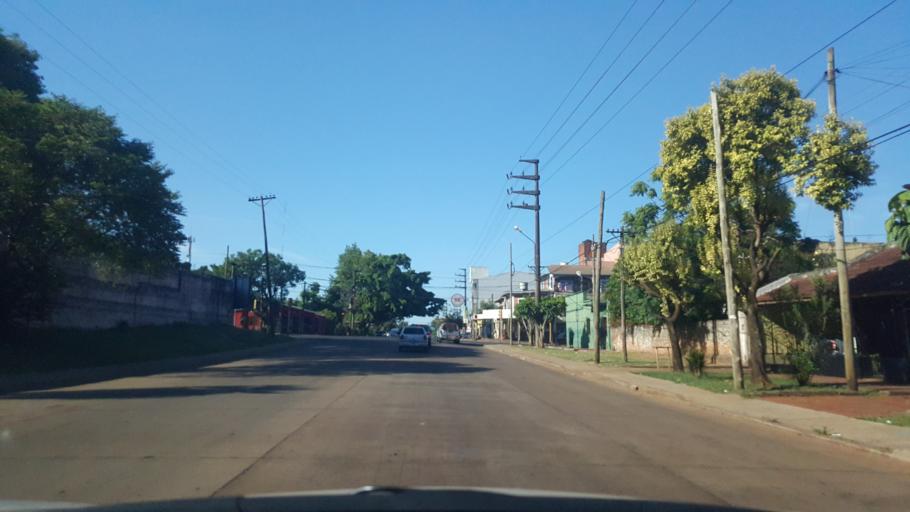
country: AR
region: Misiones
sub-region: Departamento de Capital
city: Posadas
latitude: -27.3804
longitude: -55.9108
